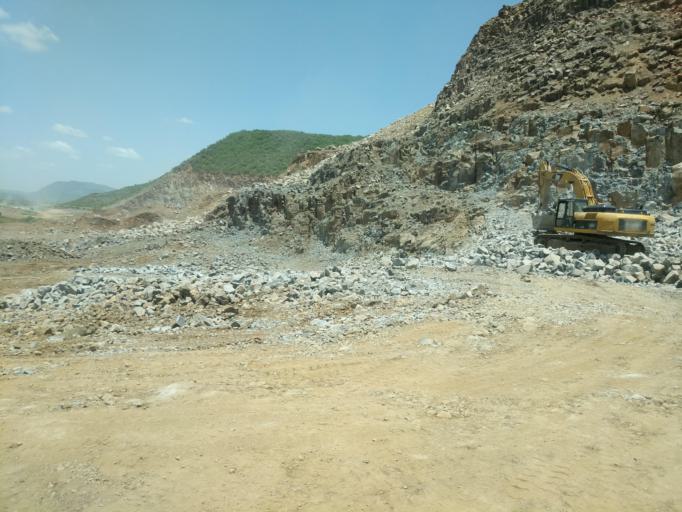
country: ET
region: Oromiya
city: Ziway
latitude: 7.9400
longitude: 38.6183
